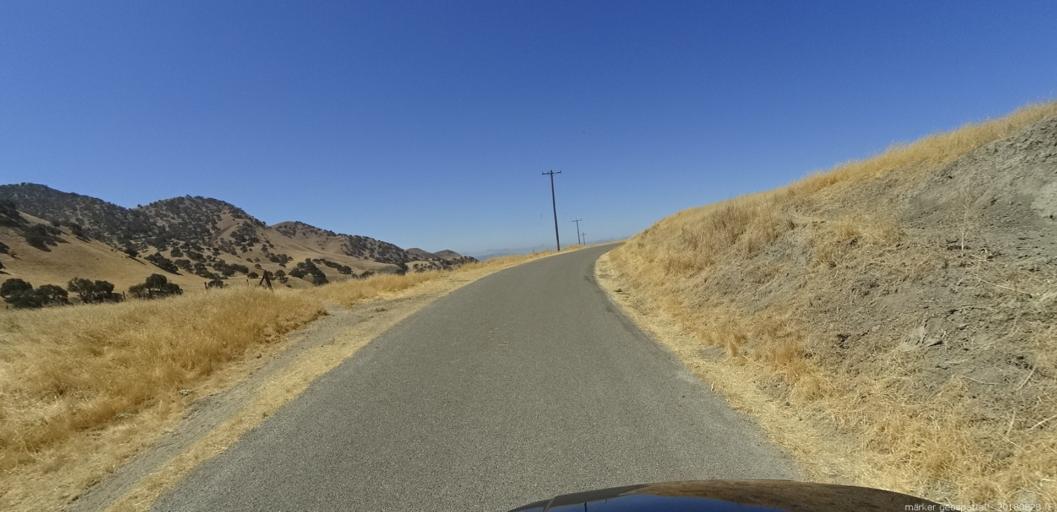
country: US
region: California
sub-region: San Luis Obispo County
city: San Miguel
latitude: 36.0637
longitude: -120.7874
